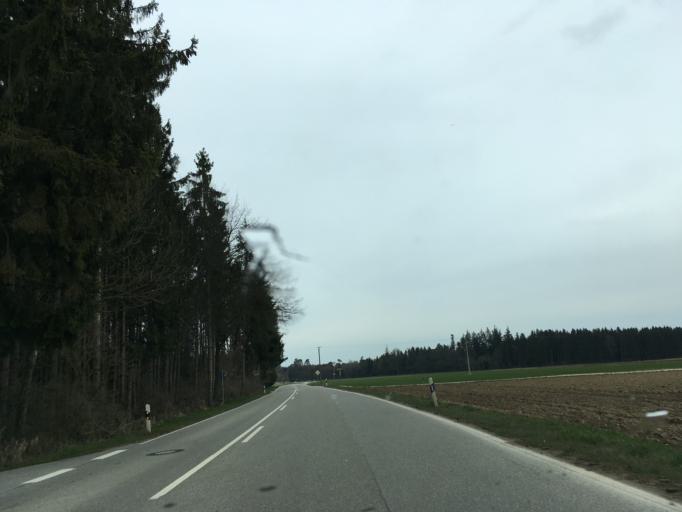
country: DE
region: Bavaria
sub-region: Upper Bavaria
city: Schnaitsee
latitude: 48.0847
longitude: 12.4096
